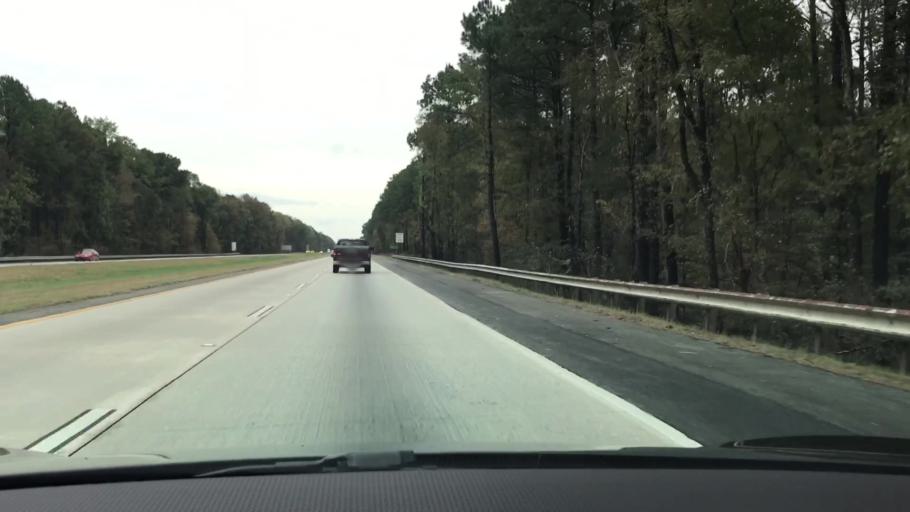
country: US
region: Georgia
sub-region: Greene County
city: Greensboro
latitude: 33.5465
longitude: -83.1906
